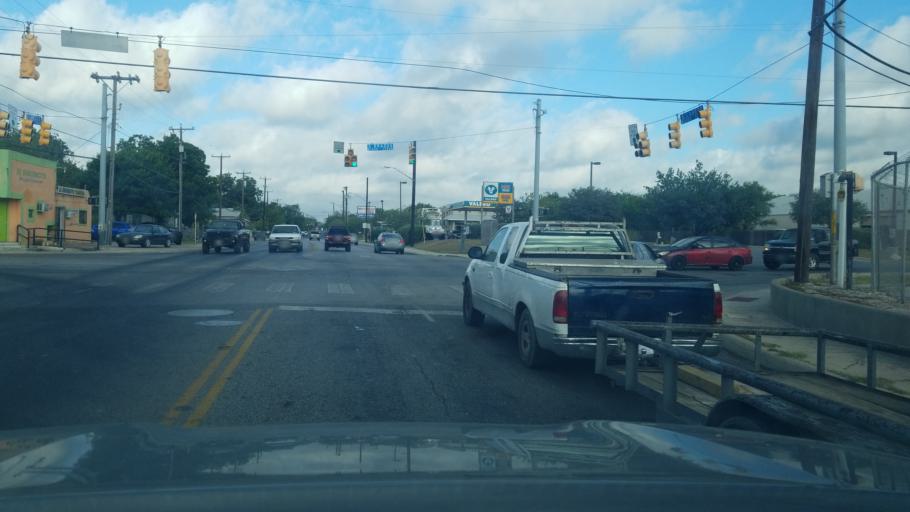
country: US
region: Texas
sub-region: Bexar County
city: San Antonio
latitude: 29.4120
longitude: -98.5149
